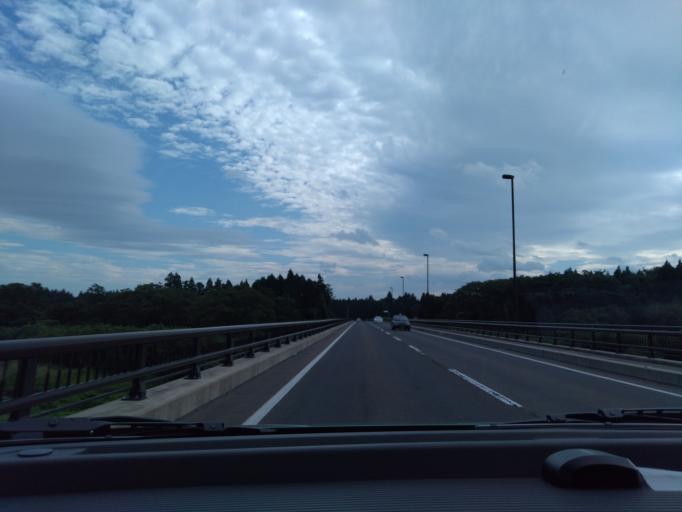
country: JP
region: Iwate
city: Hanamaki
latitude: 39.3795
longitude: 141.0570
